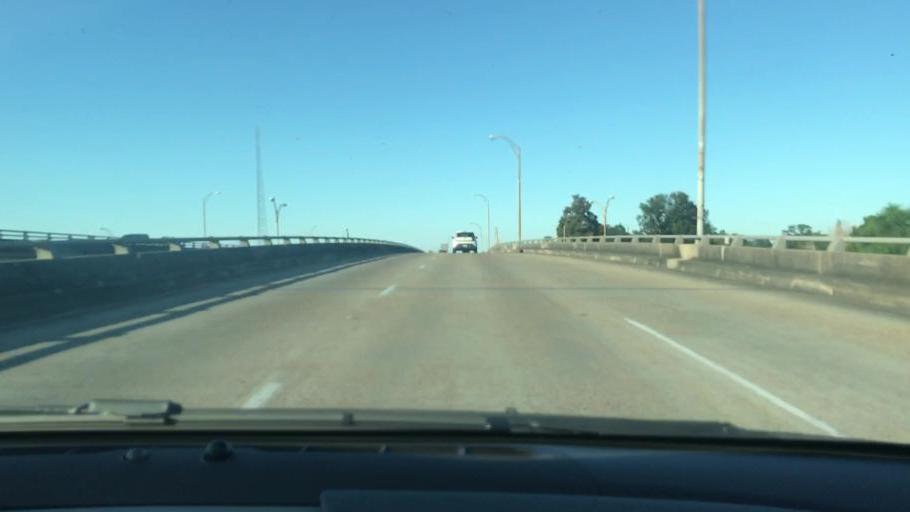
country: US
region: Louisiana
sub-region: Jefferson Parish
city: Metairie
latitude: 29.9949
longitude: -90.1157
